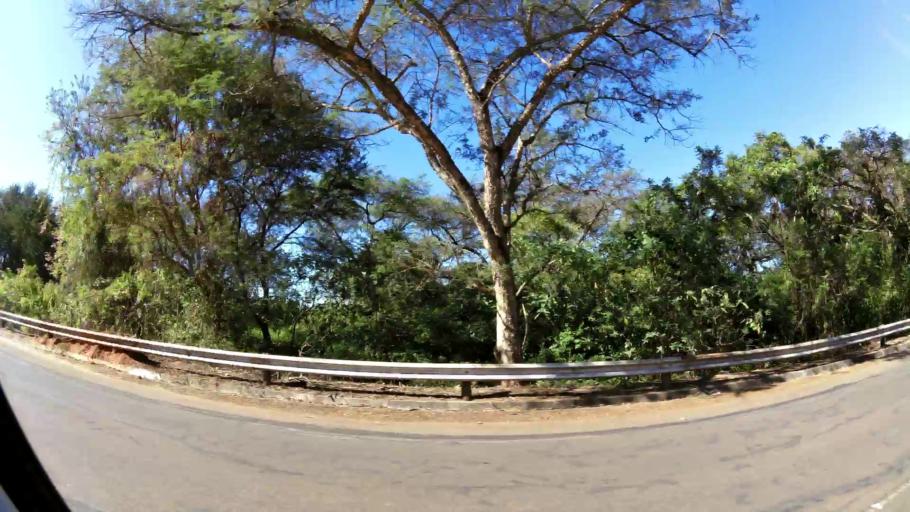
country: ZA
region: Limpopo
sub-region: Mopani District Municipality
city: Tzaneen
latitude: -23.8300
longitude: 30.1408
